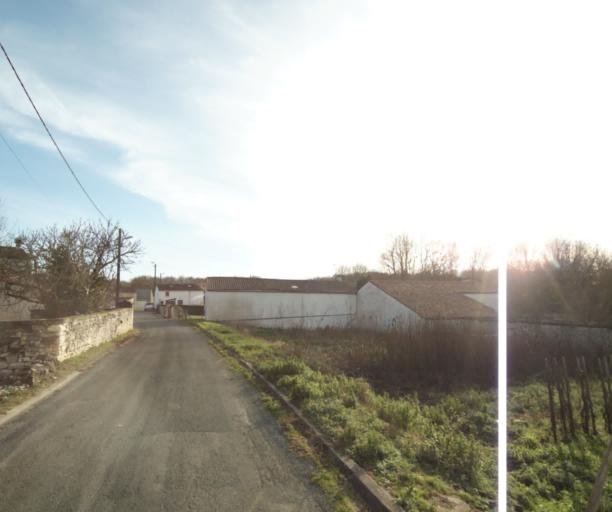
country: FR
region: Poitou-Charentes
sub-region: Departement de la Charente-Maritime
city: Fontcouverte
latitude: 45.8157
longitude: -0.5817
